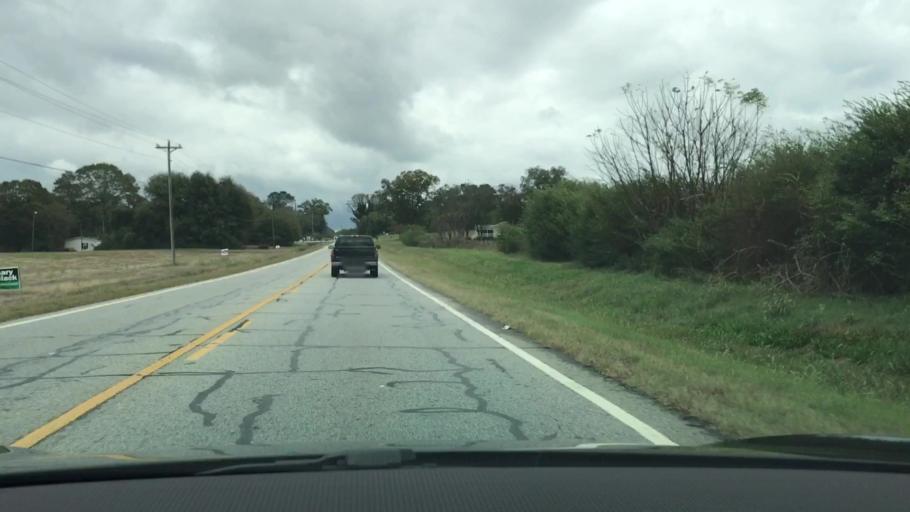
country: US
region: Georgia
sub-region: Oconee County
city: Watkinsville
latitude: 33.8399
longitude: -83.3856
